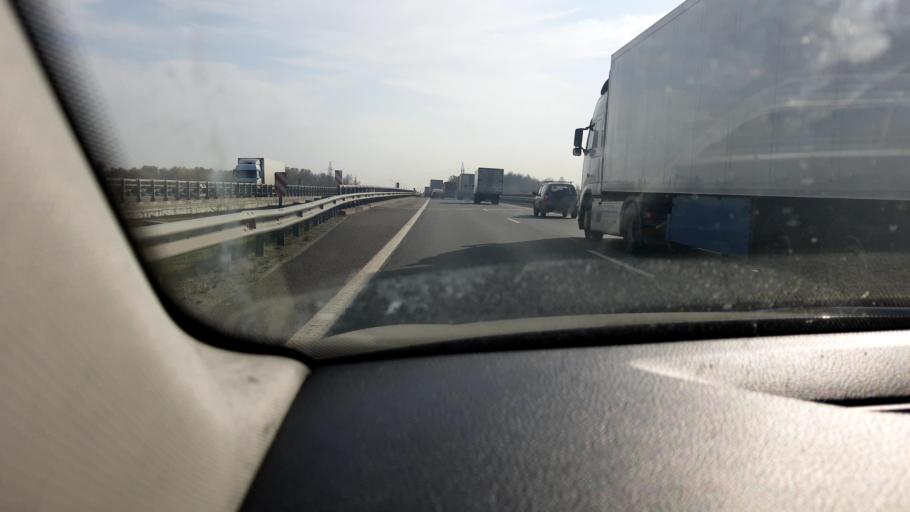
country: RU
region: Moskovskaya
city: Zhilevo
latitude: 54.9781
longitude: 37.9661
